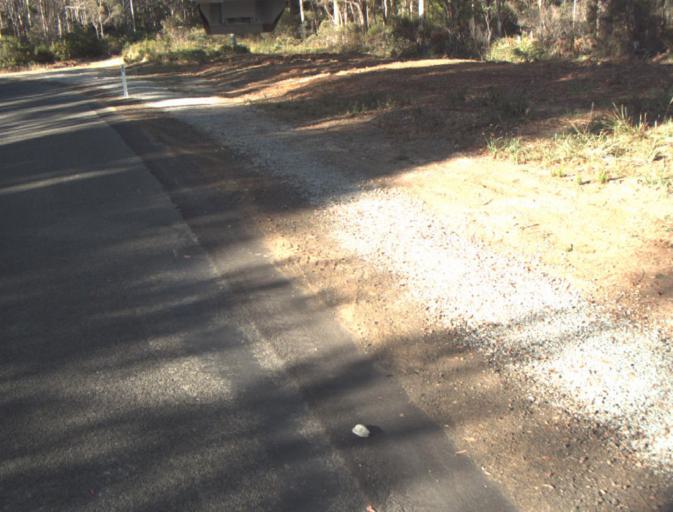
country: AU
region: Tasmania
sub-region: Launceston
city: Mayfield
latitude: -41.3119
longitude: 147.1981
